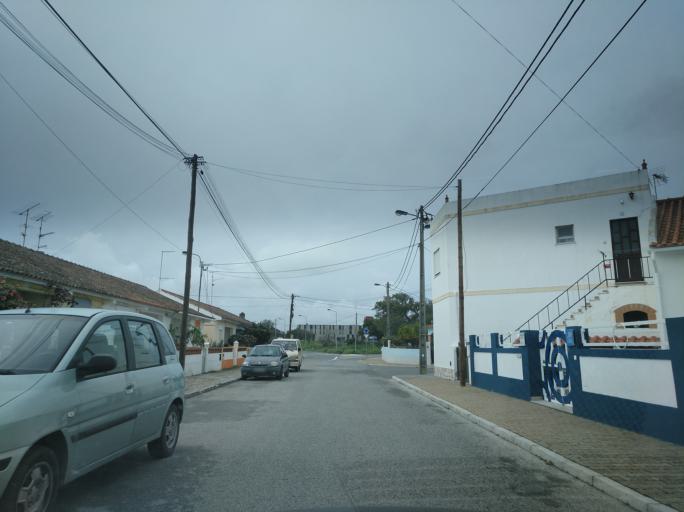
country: PT
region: Setubal
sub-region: Grandola
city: Grandola
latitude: 38.1795
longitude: -8.5718
